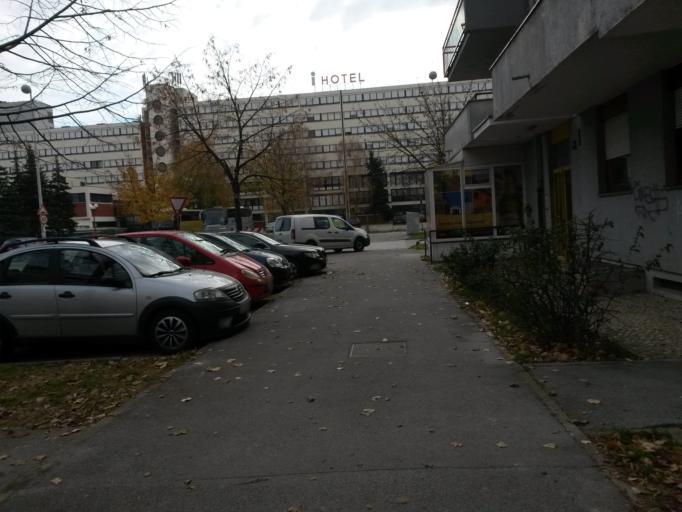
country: HR
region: Grad Zagreb
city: Novi Zagreb
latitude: 45.7727
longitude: 15.9464
